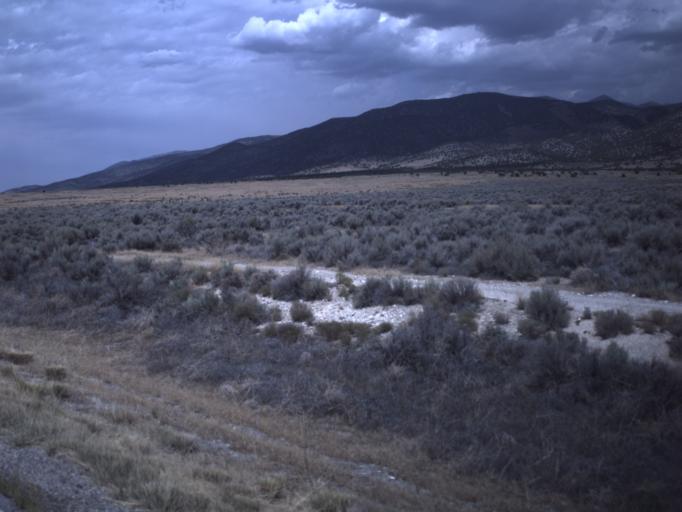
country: US
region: Utah
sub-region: Utah County
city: Eagle Mountain
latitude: 40.2501
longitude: -112.2173
